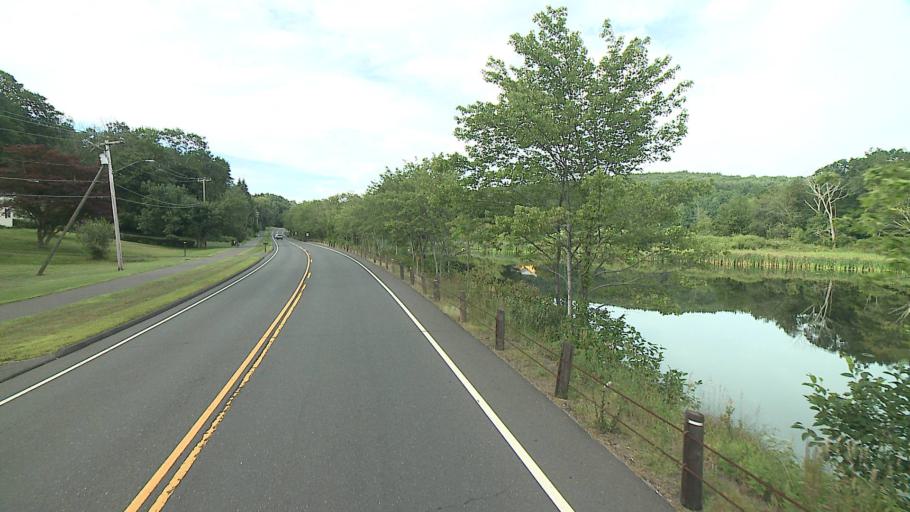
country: US
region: Connecticut
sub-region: New Haven County
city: Middlebury
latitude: 41.5368
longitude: -73.1219
